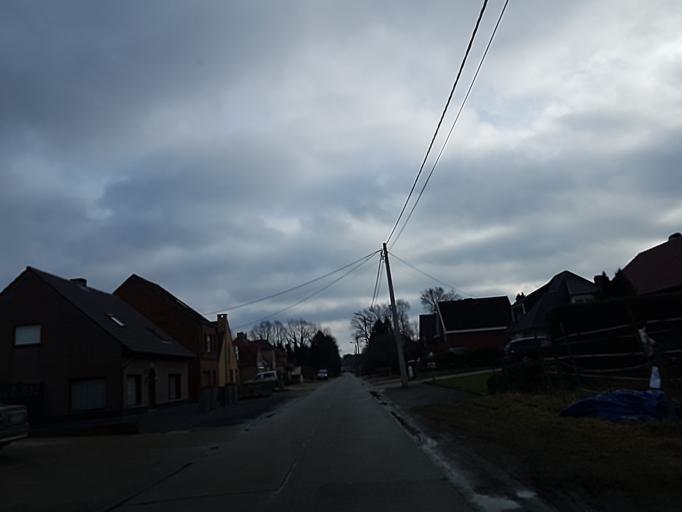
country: BE
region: Flanders
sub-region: Provincie Antwerpen
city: Hulshout
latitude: 51.0741
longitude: 4.8107
